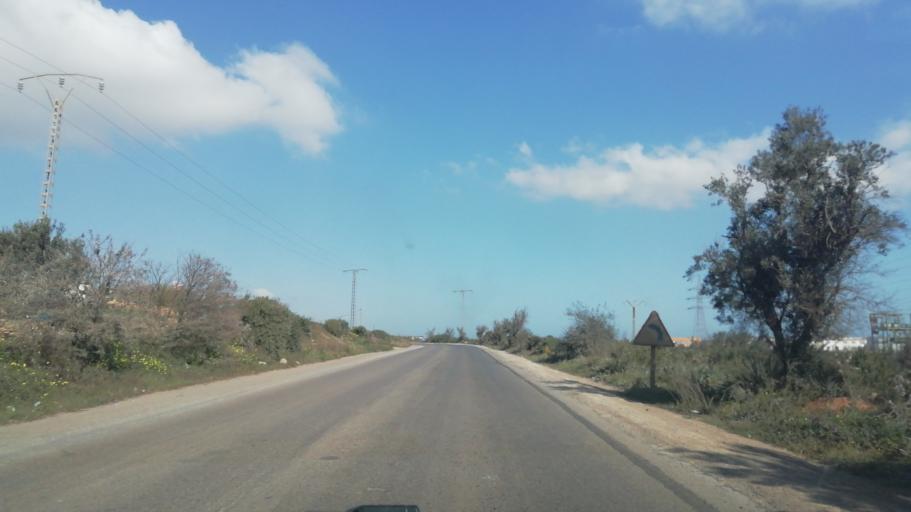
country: DZ
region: Oran
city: Ain el Bya
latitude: 35.7662
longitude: -0.2762
